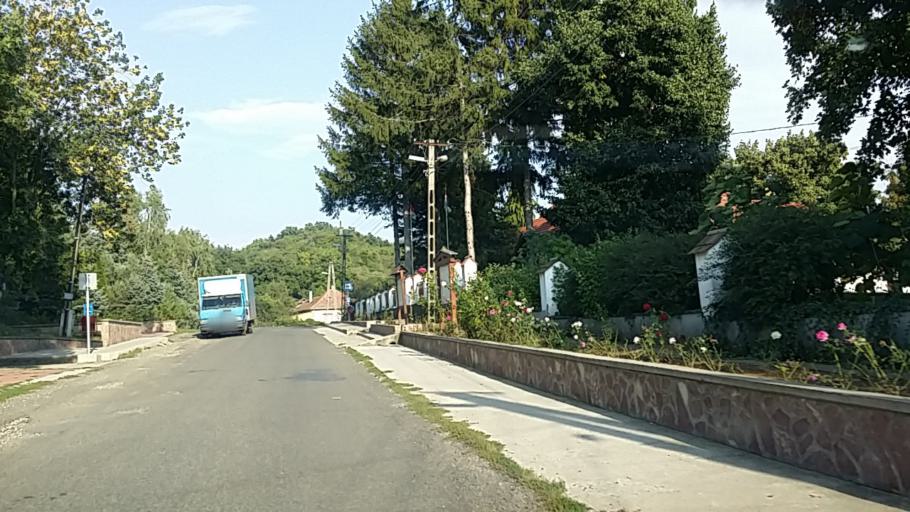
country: HU
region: Nograd
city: Bujak
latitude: 47.8629
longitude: 19.5081
